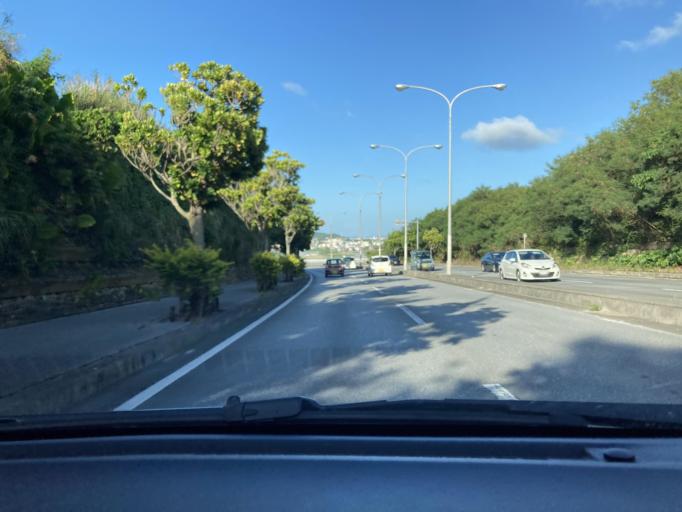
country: JP
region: Okinawa
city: Tomigusuku
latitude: 26.1641
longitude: 127.7062
